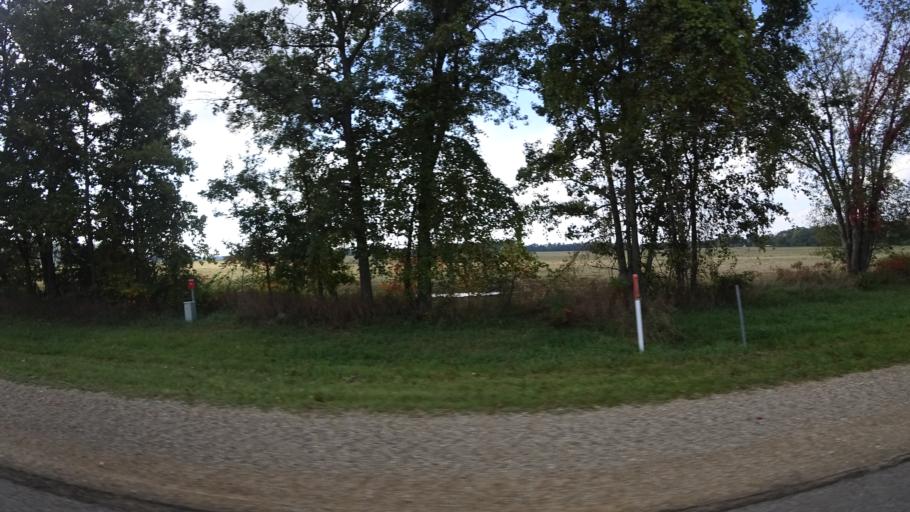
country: US
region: Michigan
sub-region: Saint Joseph County
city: Centreville
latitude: 41.9733
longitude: -85.5669
